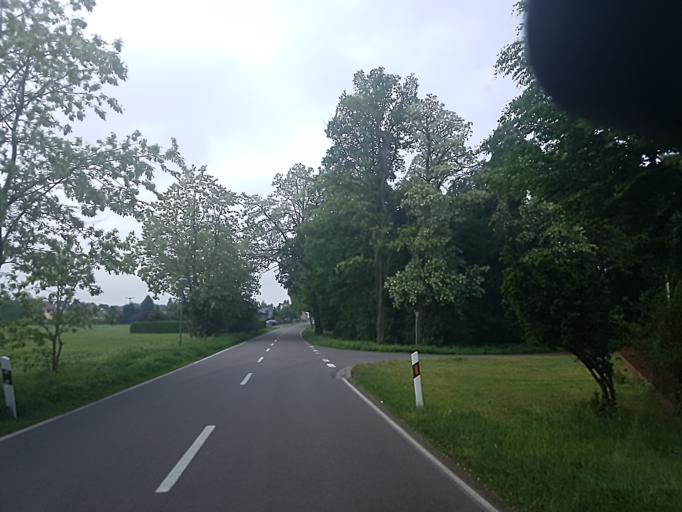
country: DE
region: Saxony-Anhalt
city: Klieken
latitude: 51.9857
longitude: 12.3542
